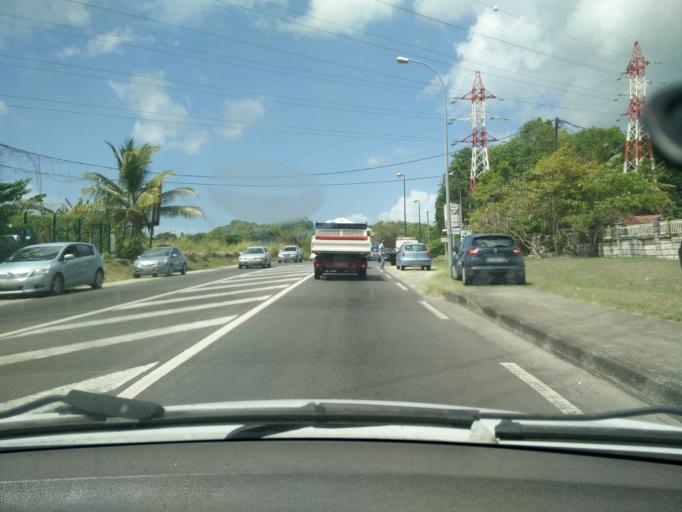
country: GP
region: Guadeloupe
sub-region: Guadeloupe
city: Les Abymes
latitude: 16.2529
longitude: -61.5145
